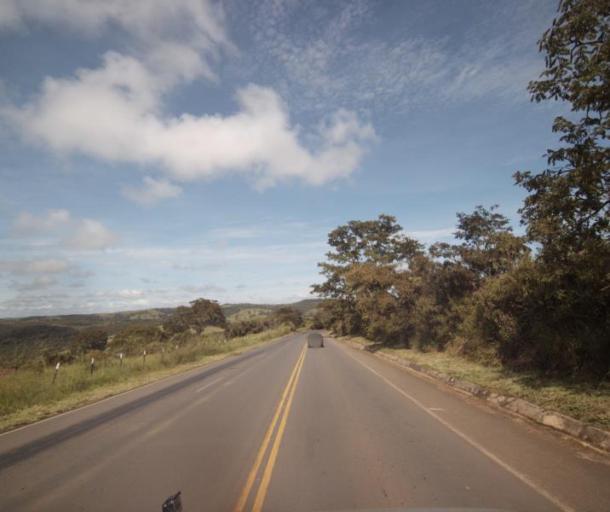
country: BR
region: Goias
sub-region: Abadiania
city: Abadiania
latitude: -16.1008
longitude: -48.8571
